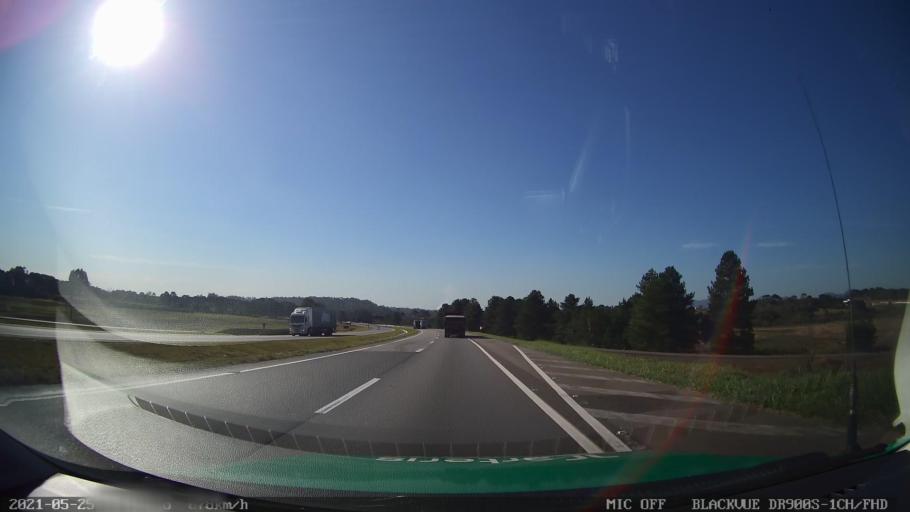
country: BR
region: Parana
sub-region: Piraquara
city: Piraquara
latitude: -25.4376
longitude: -49.0911
